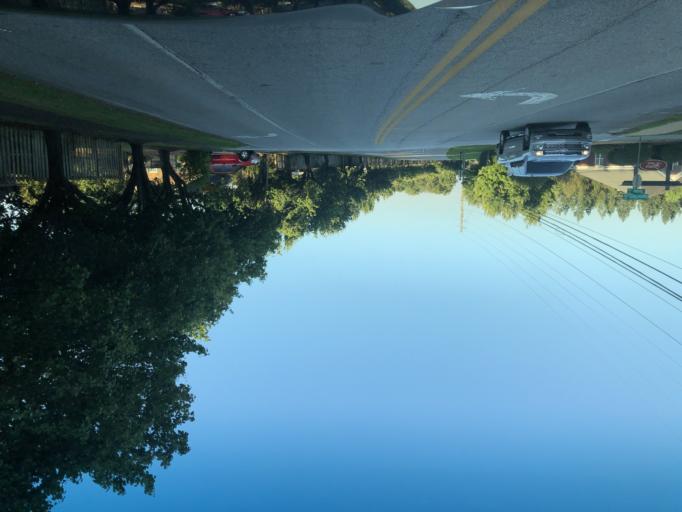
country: US
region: Georgia
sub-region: Muscogee County
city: Columbus
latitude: 32.5491
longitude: -84.8944
